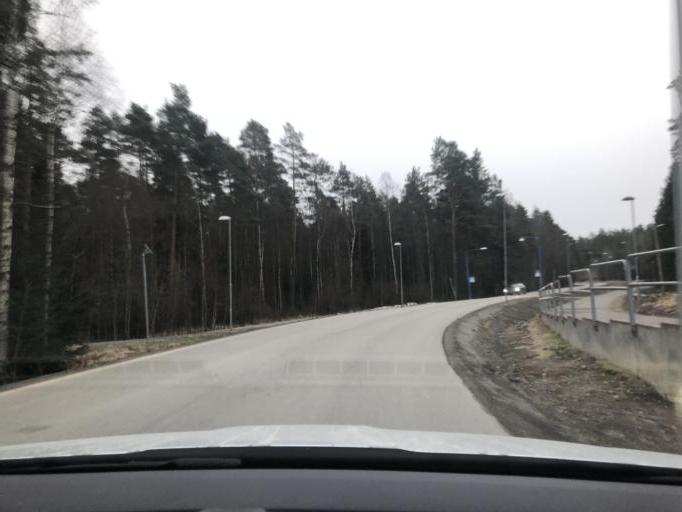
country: SE
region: Stockholm
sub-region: Botkyrka Kommun
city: Tullinge
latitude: 59.1930
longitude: 17.9086
